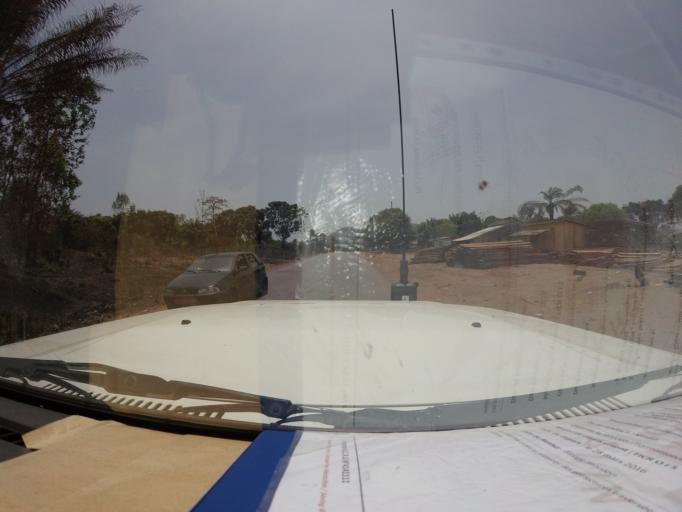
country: GN
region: Kindia
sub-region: Coyah
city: Coyah
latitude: 9.7915
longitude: -13.3054
